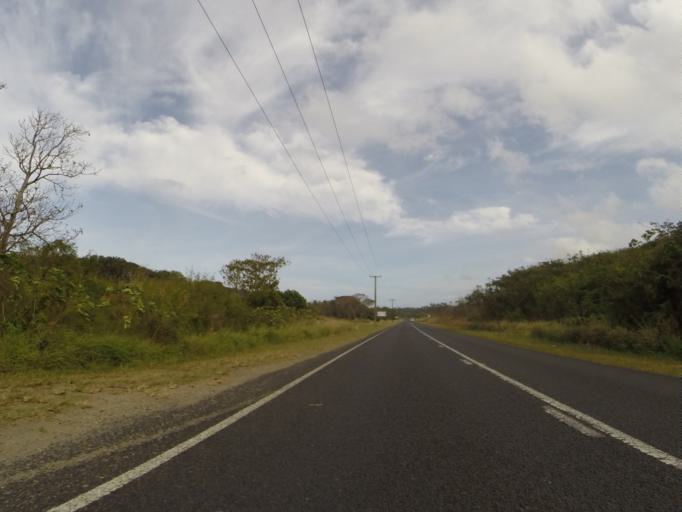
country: FJ
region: Western
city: Nadi
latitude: -18.1668
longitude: 177.4762
